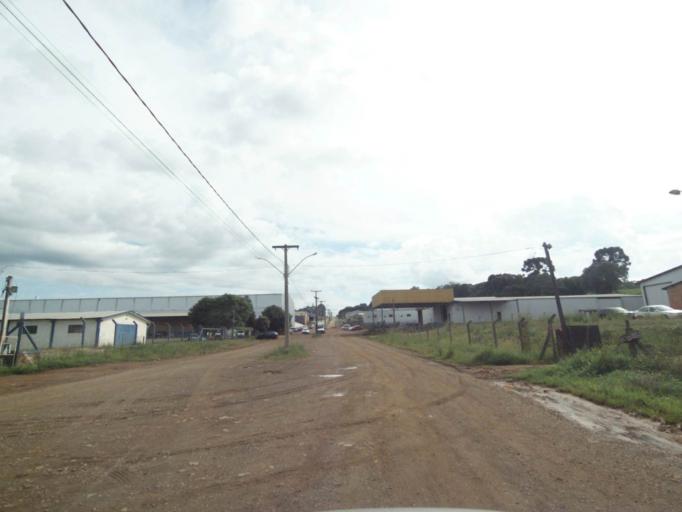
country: BR
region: Rio Grande do Sul
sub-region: Lagoa Vermelha
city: Lagoa Vermelha
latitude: -28.2322
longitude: -51.5161
